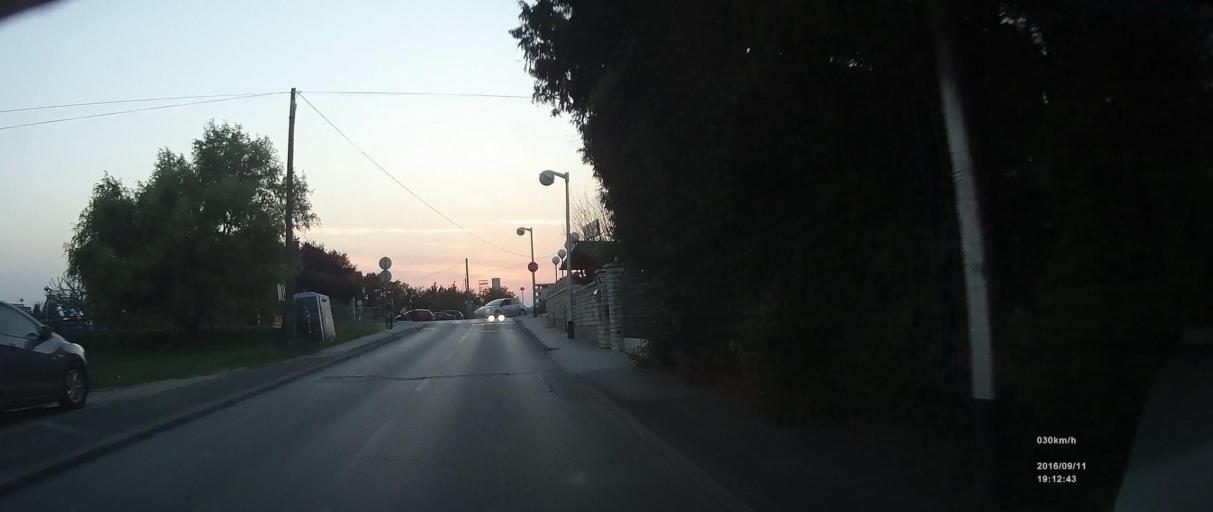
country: HR
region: Grad Zagreb
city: Stenjevec
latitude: 45.8145
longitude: 15.8701
